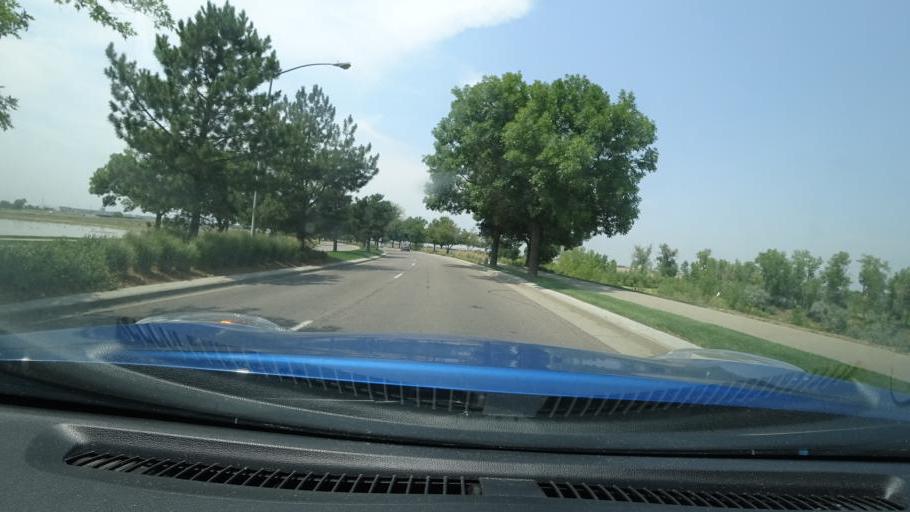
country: US
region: Colorado
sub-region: Adams County
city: Aurora
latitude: 39.7613
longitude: -104.7638
